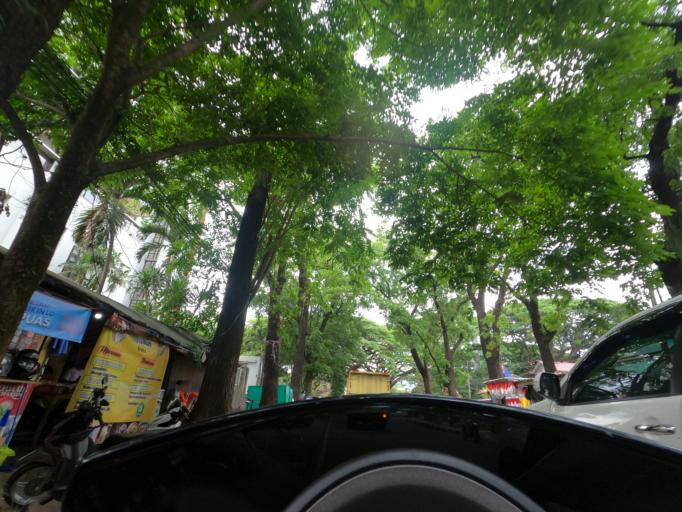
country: ID
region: West Java
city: Bandung
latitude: -6.9068
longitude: 107.6243
